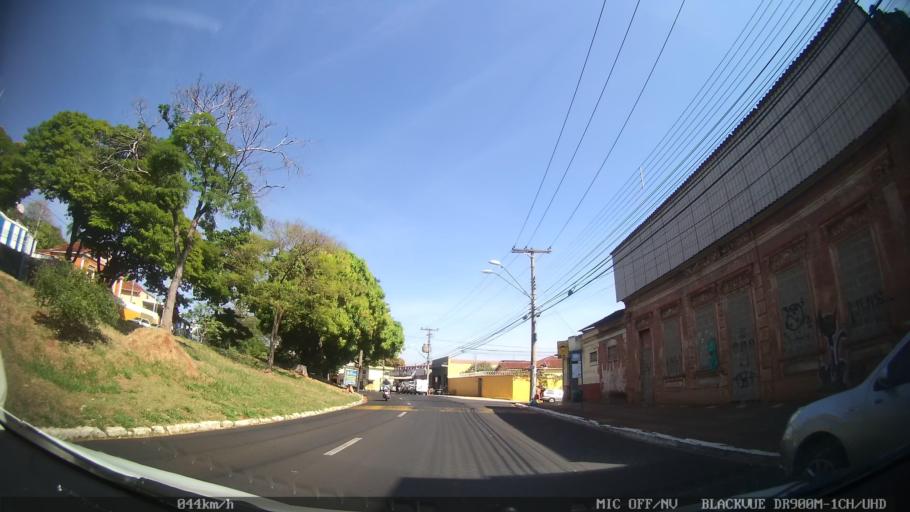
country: BR
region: Sao Paulo
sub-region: Ribeirao Preto
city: Ribeirao Preto
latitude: -21.1804
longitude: -47.8179
